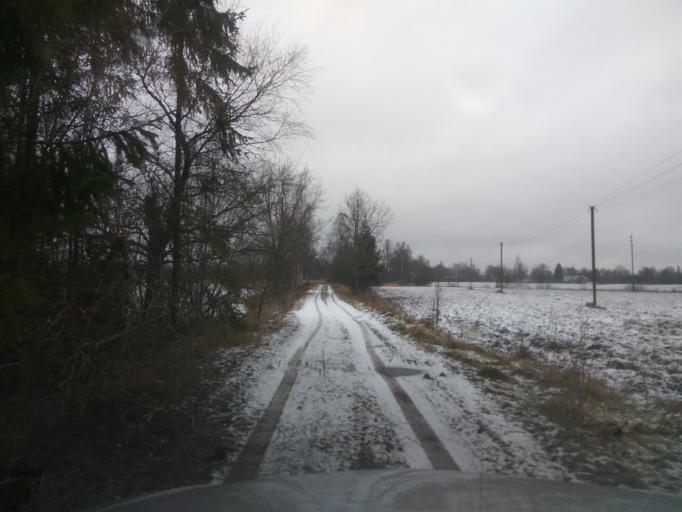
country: LV
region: Broceni
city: Broceni
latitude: 56.8478
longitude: 22.3884
